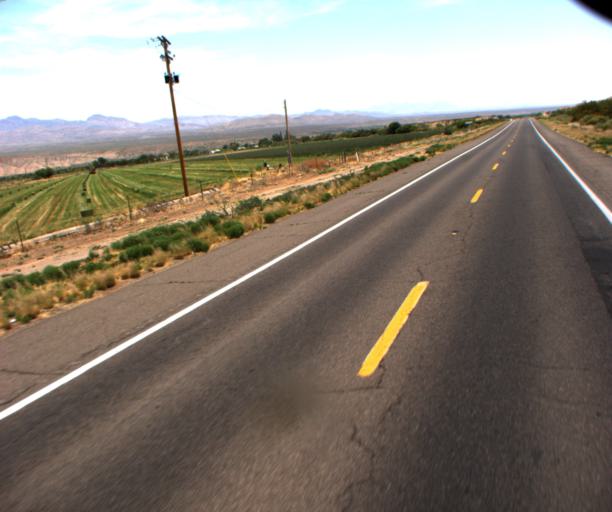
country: US
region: Arizona
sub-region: Graham County
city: Bylas
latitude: 33.0765
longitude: -110.0327
